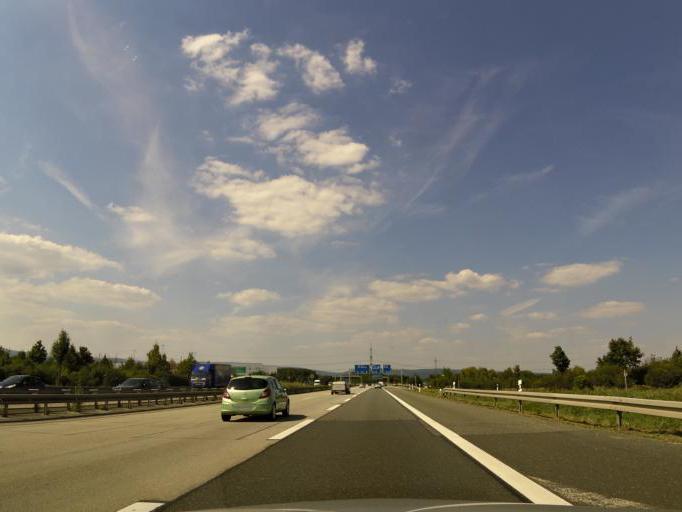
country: DE
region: Hesse
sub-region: Regierungsbezirk Darmstadt
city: Bad Homburg vor der Hoehe
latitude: 50.1947
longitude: 8.6525
